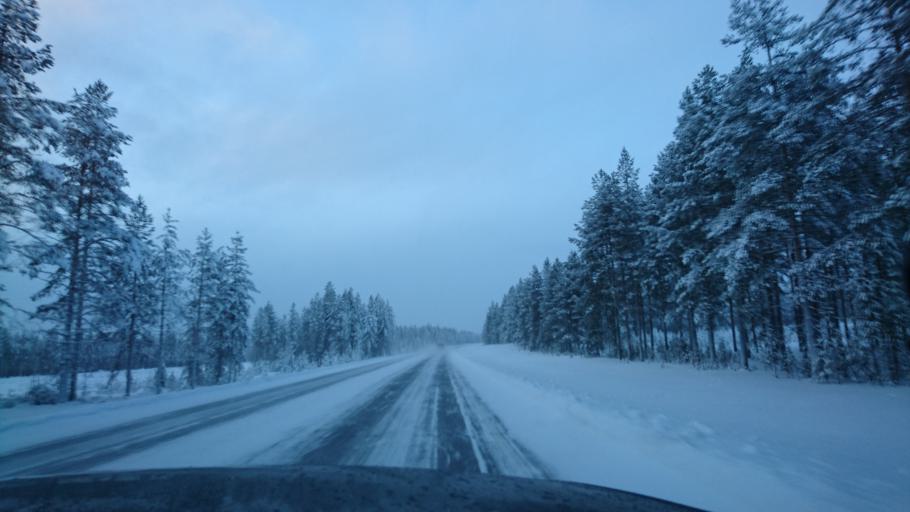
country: FI
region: Kainuu
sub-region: Kehys-Kainuu
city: Puolanka
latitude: 65.4357
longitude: 27.5905
